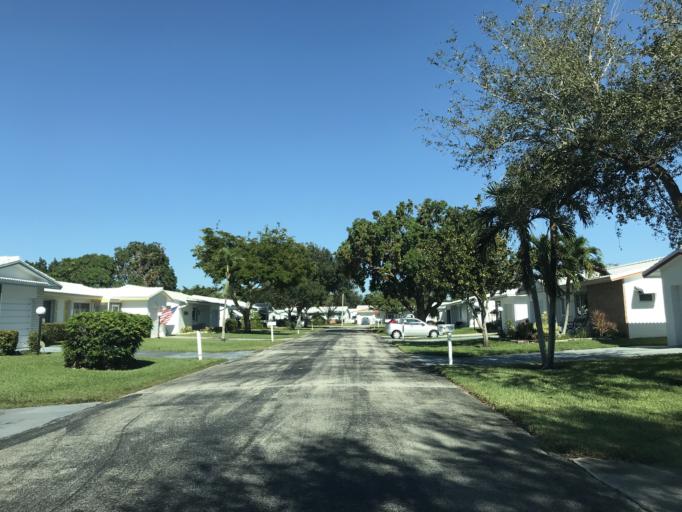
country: US
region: Florida
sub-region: Broward County
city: Plantation
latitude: 26.1396
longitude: -80.2687
